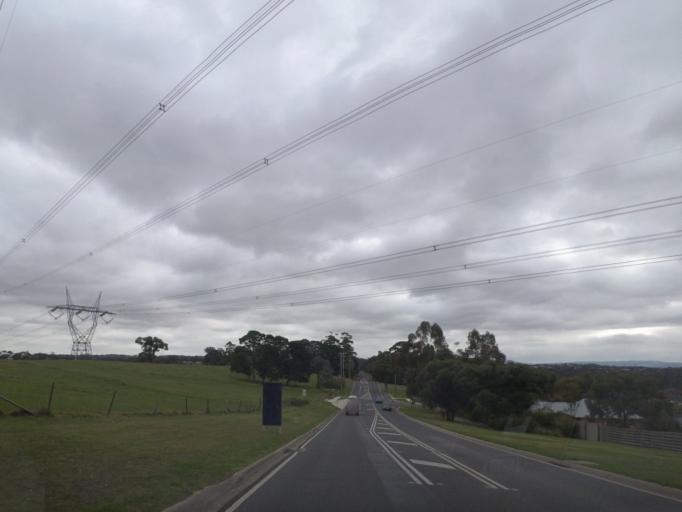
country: AU
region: Victoria
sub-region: Nillumbik
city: Eltham North
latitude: -37.6837
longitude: 145.1435
